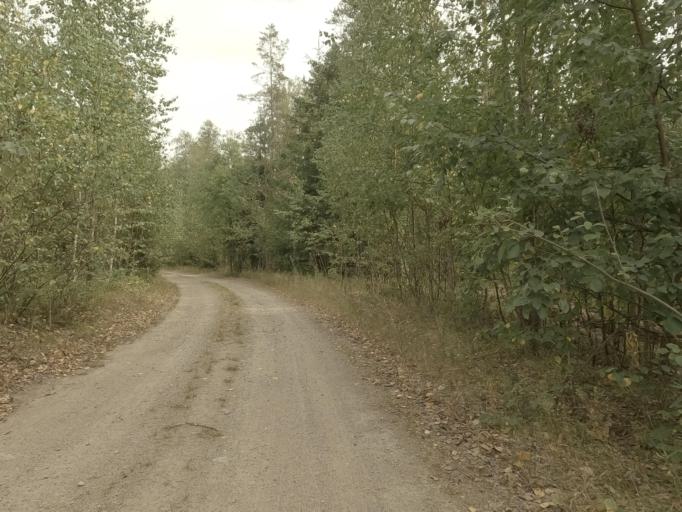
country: RU
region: Leningrad
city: Kamennogorsk
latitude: 61.0184
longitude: 29.1926
